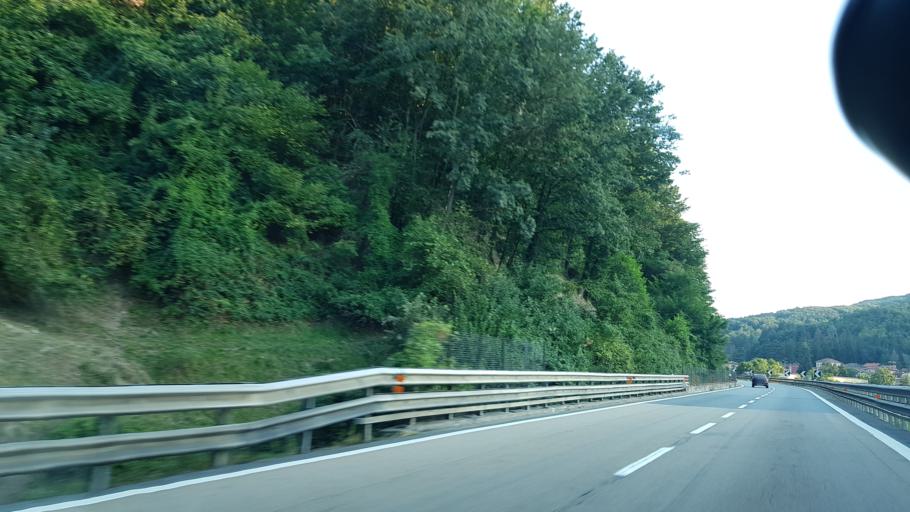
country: IT
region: Liguria
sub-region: Provincia di Genova
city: Borgo Fornari-Pieve
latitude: 44.5930
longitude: 8.9413
